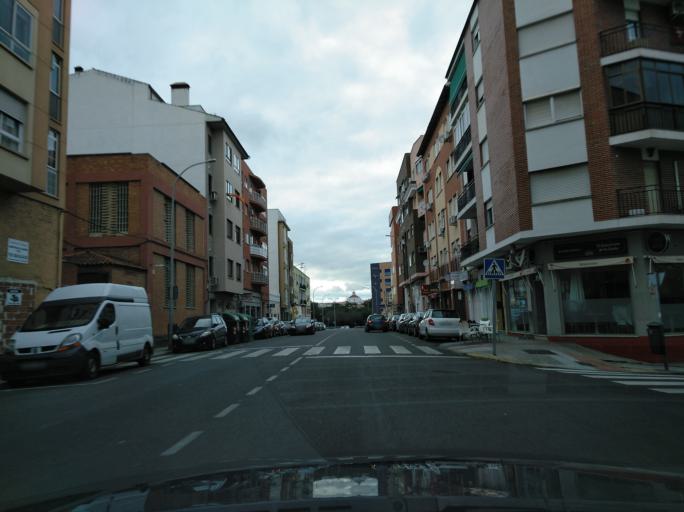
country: ES
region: Extremadura
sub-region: Provincia de Badajoz
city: Badajoz
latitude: 38.8770
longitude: -6.9594
